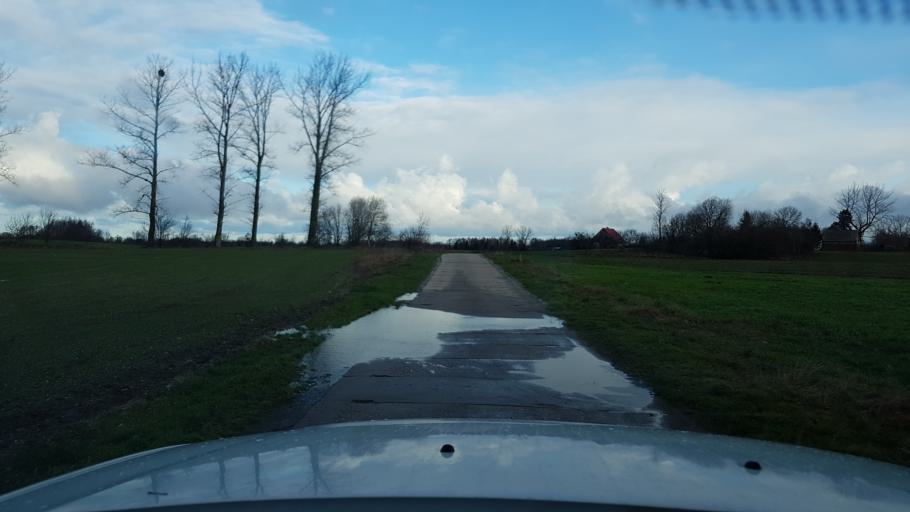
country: PL
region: West Pomeranian Voivodeship
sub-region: Powiat gryficki
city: Brojce
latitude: 54.0467
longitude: 15.3936
